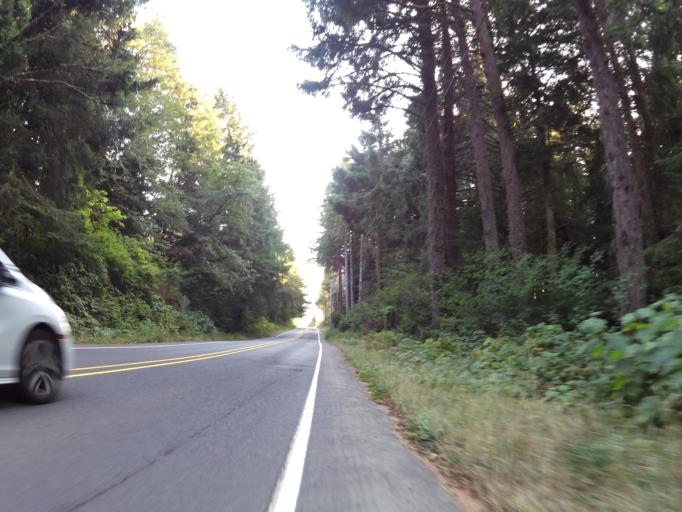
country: US
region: Oregon
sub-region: Lincoln County
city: Lincoln City
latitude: 44.9645
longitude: -123.9974
